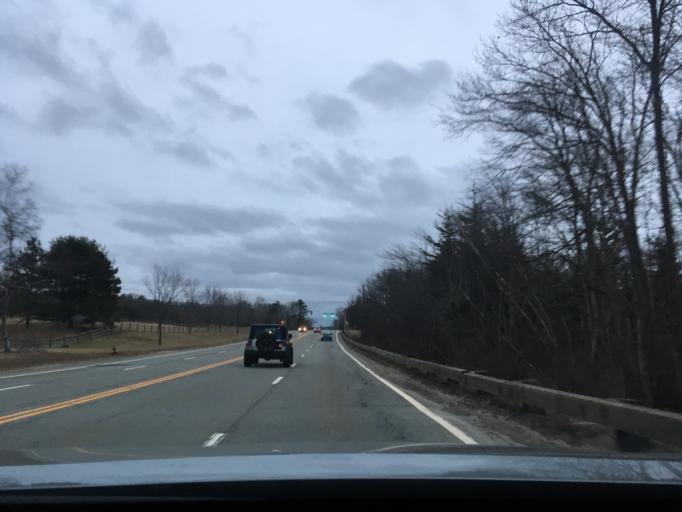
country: US
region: Rhode Island
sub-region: Providence County
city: Smithfield
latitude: 41.9236
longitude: -71.5294
